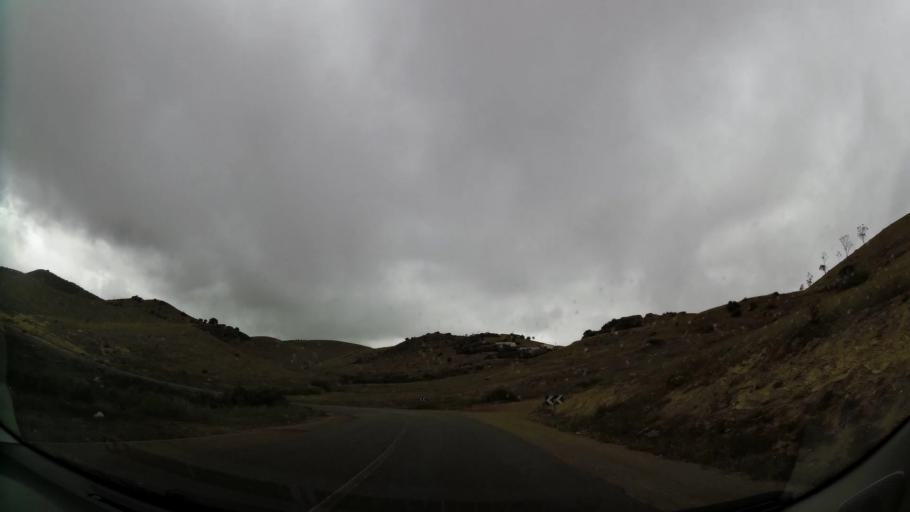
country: MA
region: Oriental
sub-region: Nador
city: Midar
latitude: 35.0660
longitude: -3.4709
